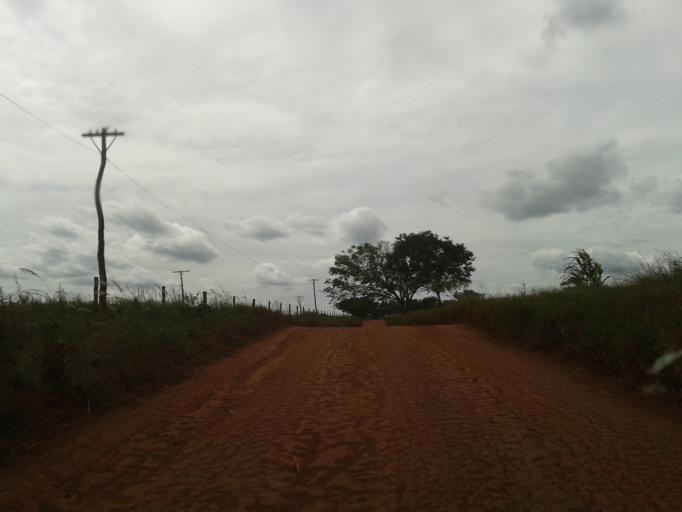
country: BR
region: Minas Gerais
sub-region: Centralina
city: Centralina
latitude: -18.7631
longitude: -49.2211
